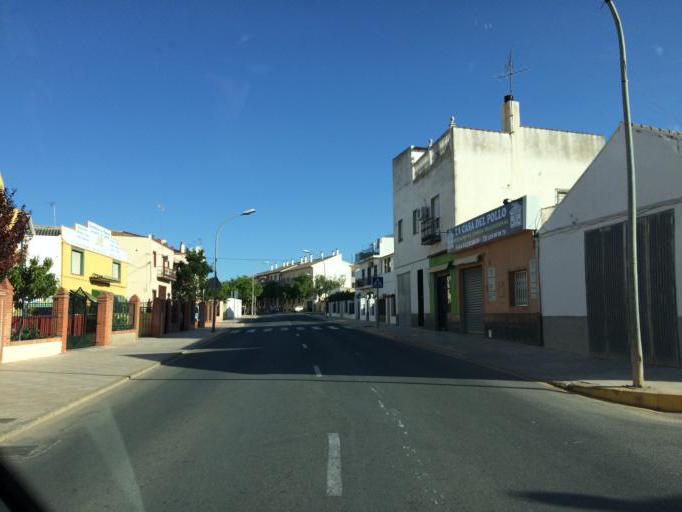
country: ES
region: Andalusia
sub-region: Provincia de Malaga
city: Campillos
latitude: 37.0470
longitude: -4.8658
